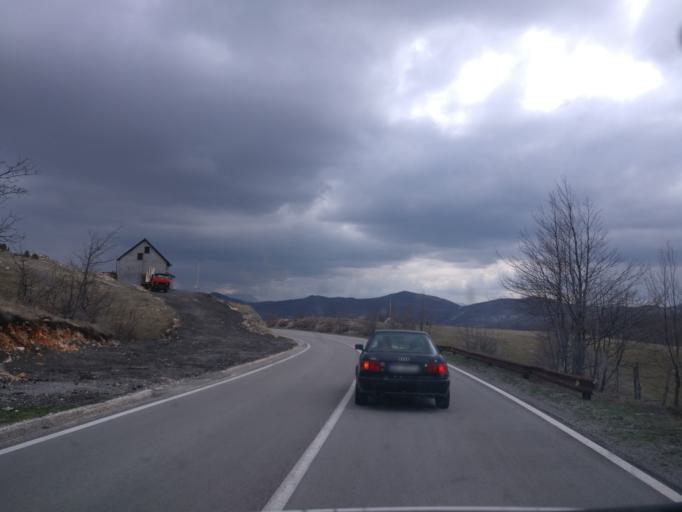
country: ME
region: Opstina Niksic
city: Niksic
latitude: 42.9320
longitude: 18.9353
